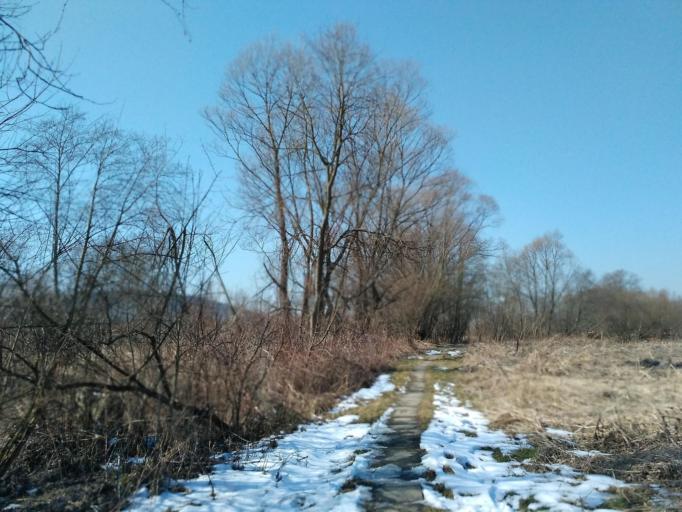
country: PL
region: Subcarpathian Voivodeship
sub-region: Powiat brzozowski
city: Domaradz
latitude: 49.7900
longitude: 21.9544
